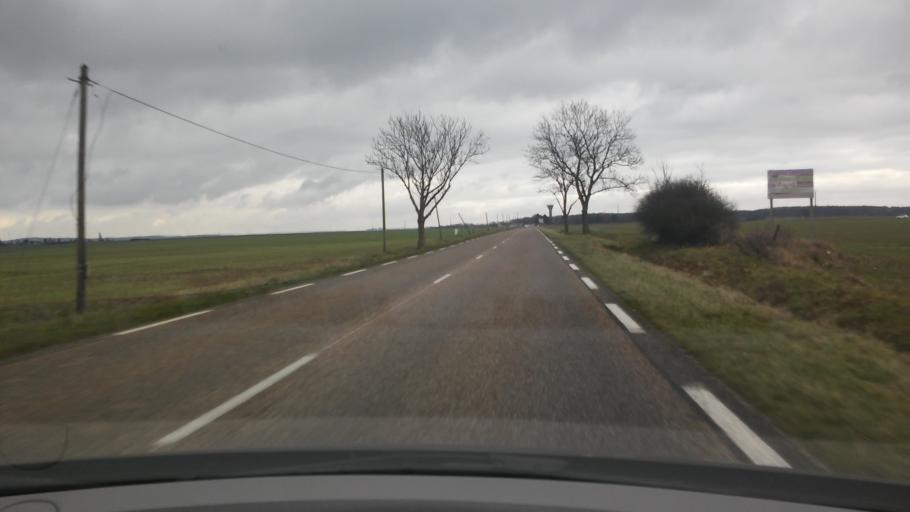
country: FR
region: Lorraine
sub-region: Departement de la Moselle
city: Retonfey
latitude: 49.1178
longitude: 6.3339
